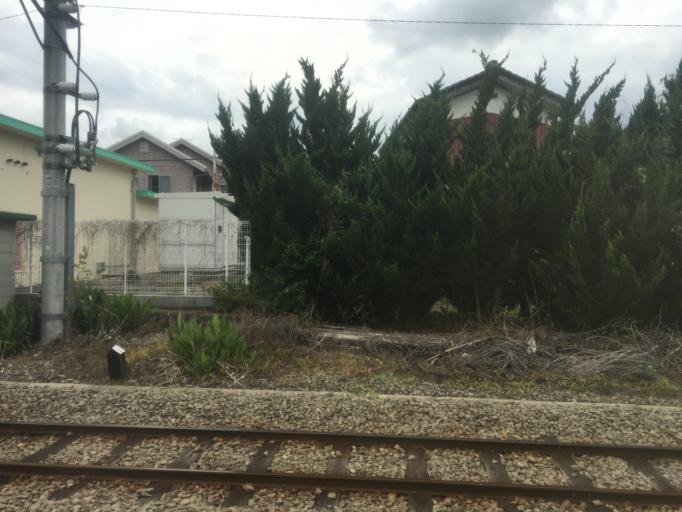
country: JP
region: Gunma
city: Fujioka
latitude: 36.2774
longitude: 139.0382
